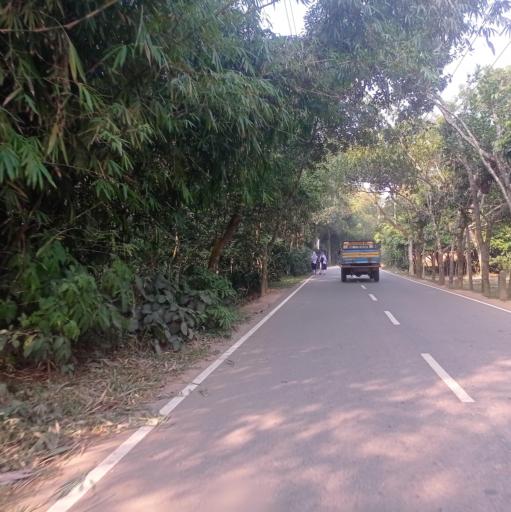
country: BD
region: Dhaka
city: Bhairab Bazar
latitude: 24.0679
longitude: 90.8416
